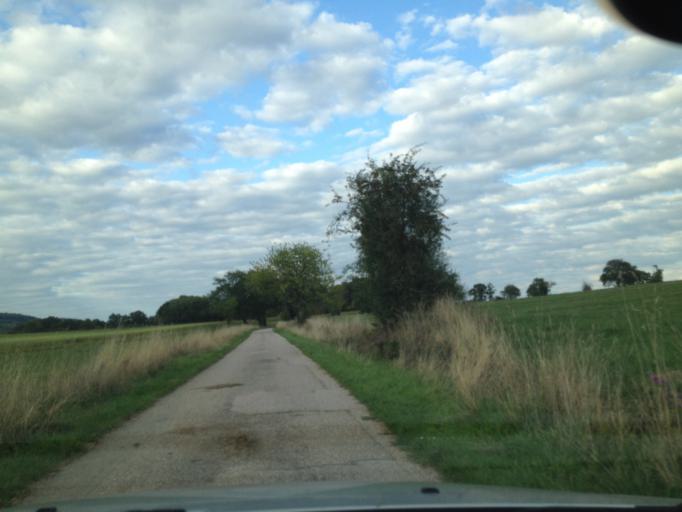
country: FR
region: Lorraine
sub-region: Departement des Vosges
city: Bains-les-Bains
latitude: 47.9836
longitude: 6.1868
